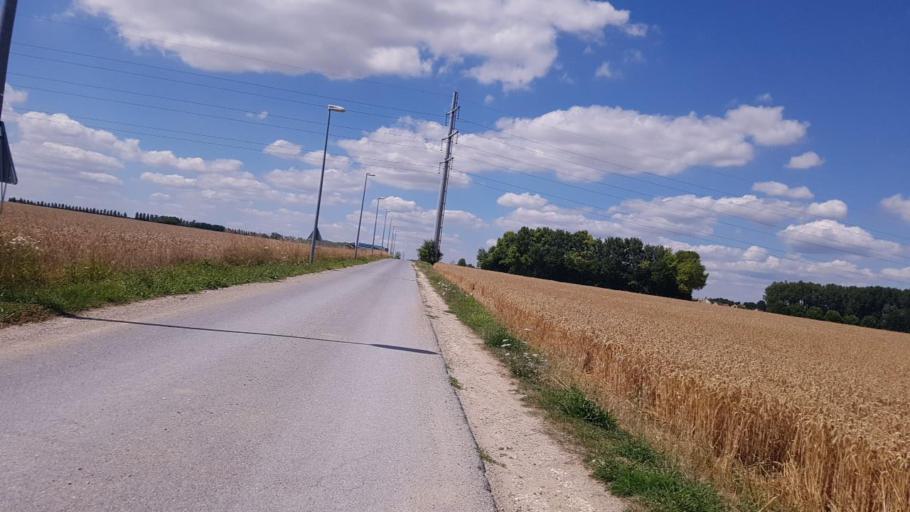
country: FR
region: Ile-de-France
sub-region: Departement de Seine-et-Marne
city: Claye-Souilly
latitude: 48.9816
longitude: 2.6718
